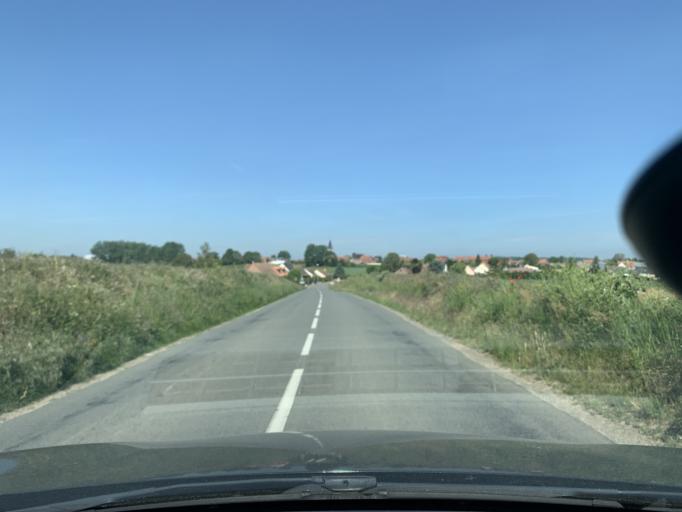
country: FR
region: Nord-Pas-de-Calais
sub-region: Departement du Nord
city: Marcoing
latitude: 50.1449
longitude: 3.1699
